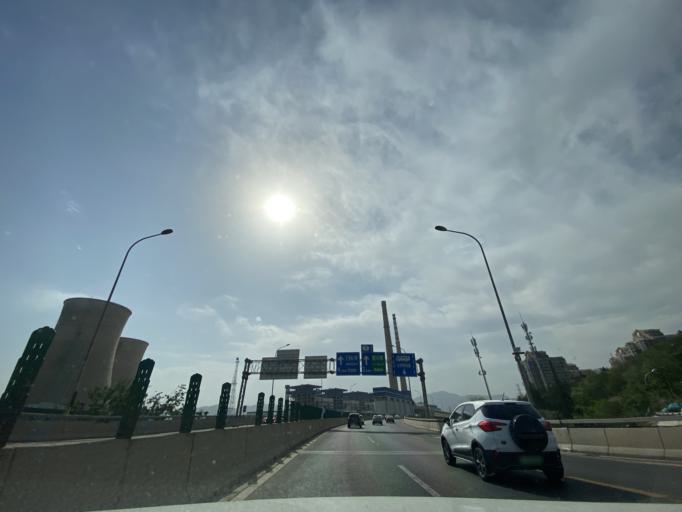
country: CN
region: Beijing
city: Guangning
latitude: 39.9228
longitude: 116.1440
